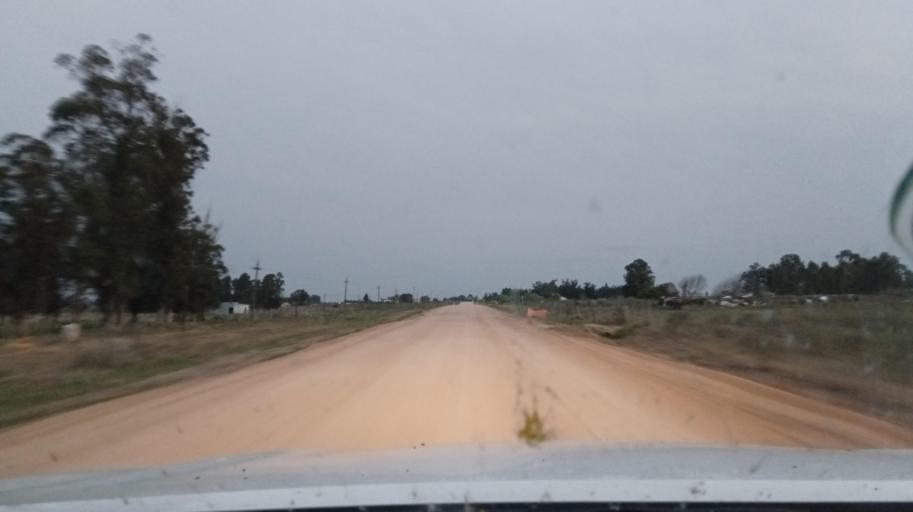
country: UY
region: Canelones
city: Santa Rosa
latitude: -34.5334
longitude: -56.0992
